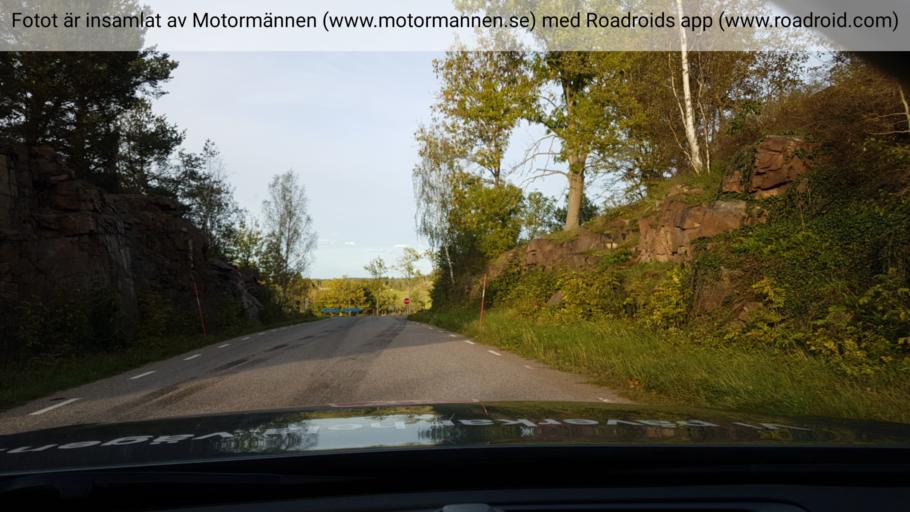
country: SE
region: Kalmar
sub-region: Vasterviks Kommun
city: Forserum
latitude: 57.9373
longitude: 16.4613
